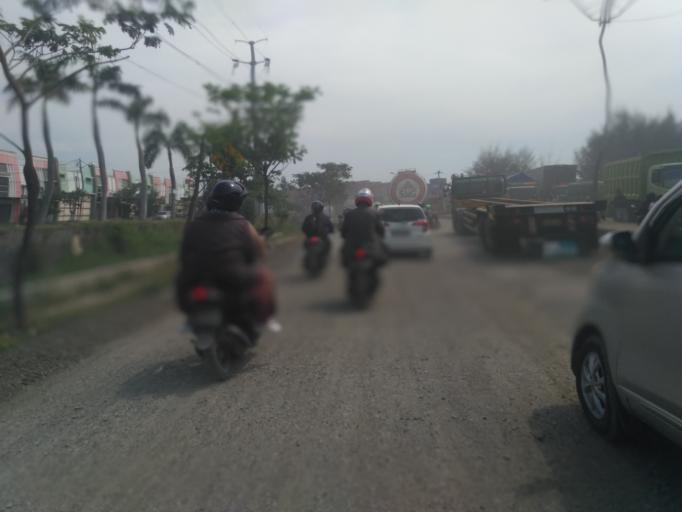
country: ID
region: Central Java
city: Semarang
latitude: -6.9541
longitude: 110.4123
